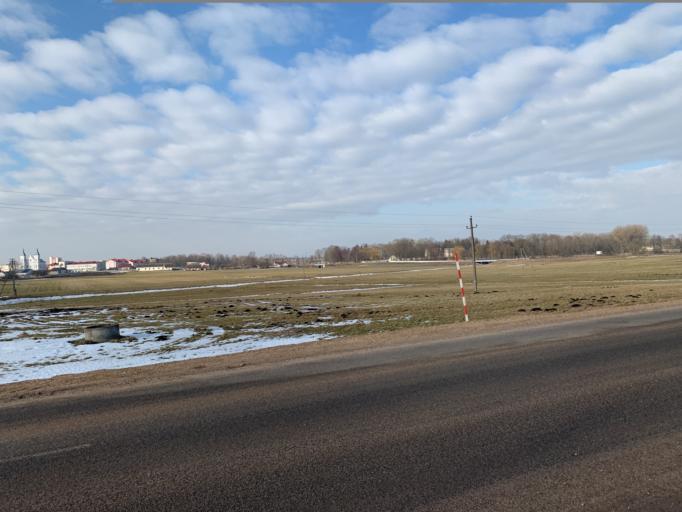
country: BY
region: Minsk
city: Snow
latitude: 53.2171
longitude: 26.4173
